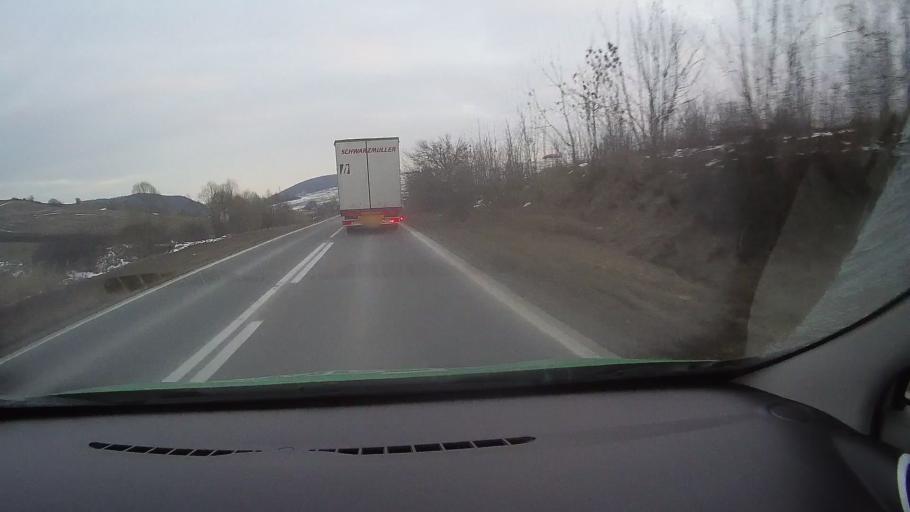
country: RO
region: Harghita
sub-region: Comuna Lupeni
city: Lupeni
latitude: 46.3491
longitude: 25.2636
